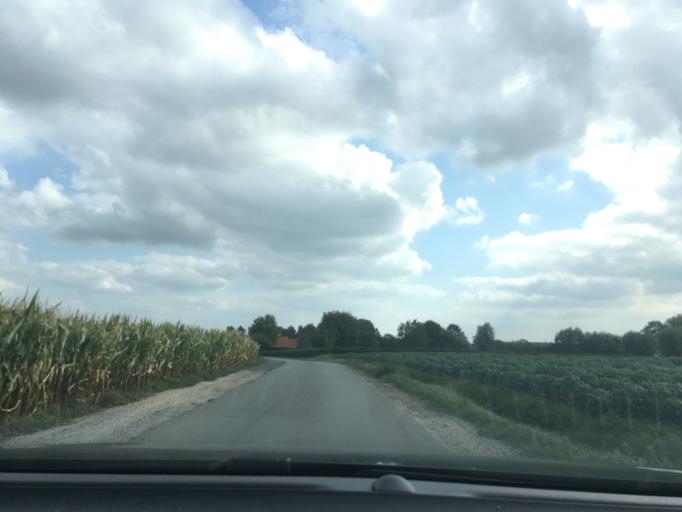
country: BE
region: Flanders
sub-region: Provincie West-Vlaanderen
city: Ieper
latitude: 50.8763
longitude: 2.9261
